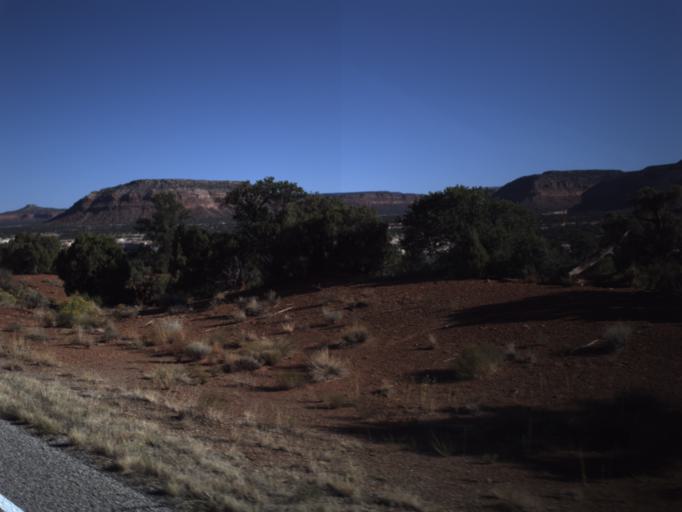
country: US
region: Utah
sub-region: San Juan County
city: Blanding
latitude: 37.6112
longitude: -110.0810
